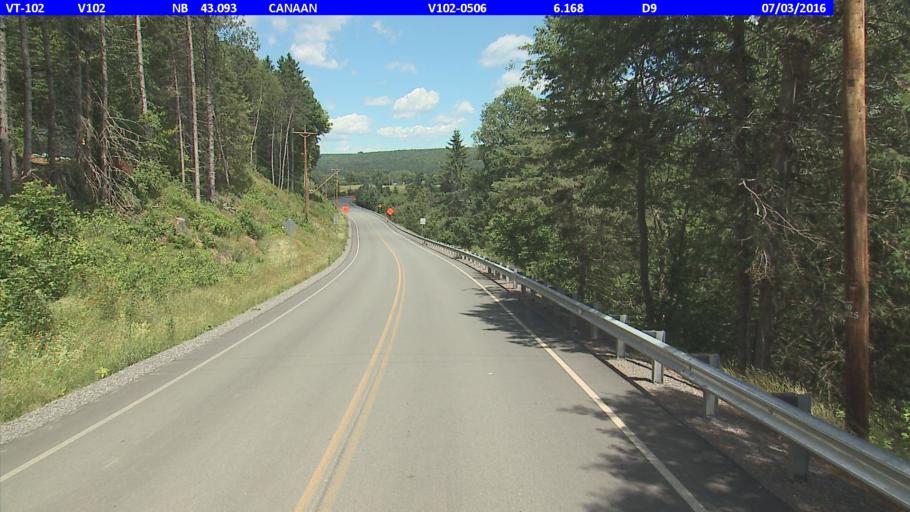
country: US
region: New Hampshire
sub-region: Coos County
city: Colebrook
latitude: 44.9875
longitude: -71.5420
